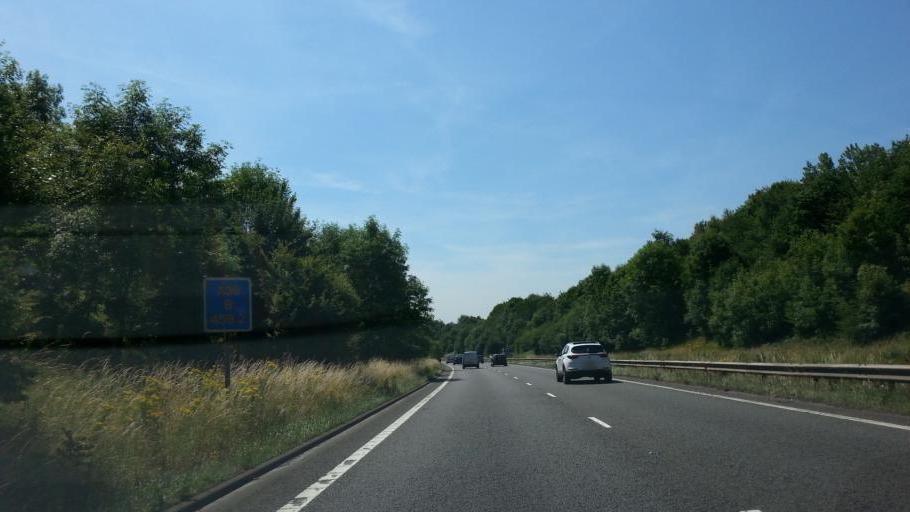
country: GB
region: England
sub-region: Derbyshire
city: Heage
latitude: 53.0326
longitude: -1.4401
